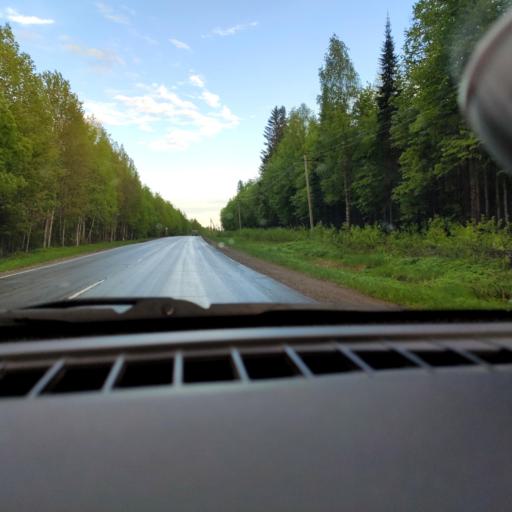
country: RU
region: Perm
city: Perm
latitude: 58.2113
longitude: 56.1853
